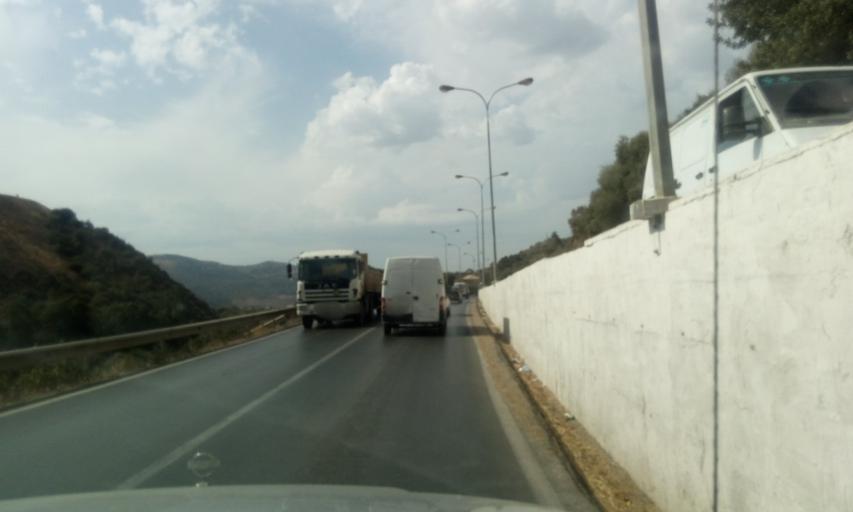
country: DZ
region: Bejaia
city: Seddouk
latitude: 36.6070
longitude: 4.6817
